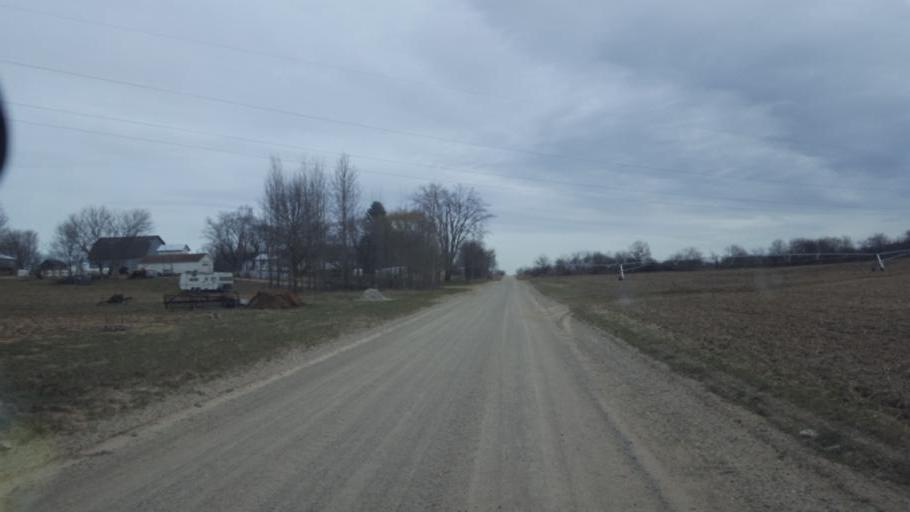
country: US
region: Michigan
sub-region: Montcalm County
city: Edmore
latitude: 43.4513
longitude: -85.0184
